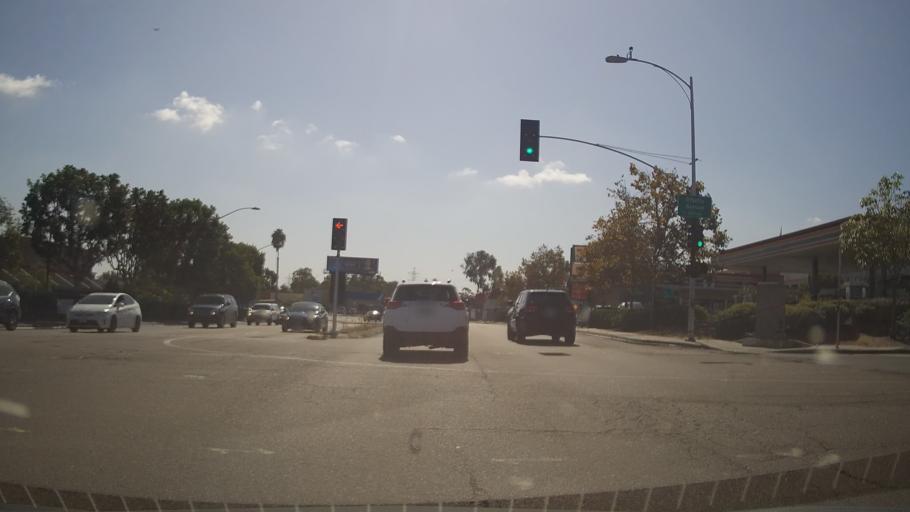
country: US
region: California
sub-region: San Diego County
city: San Diego
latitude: 32.8174
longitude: -117.1548
